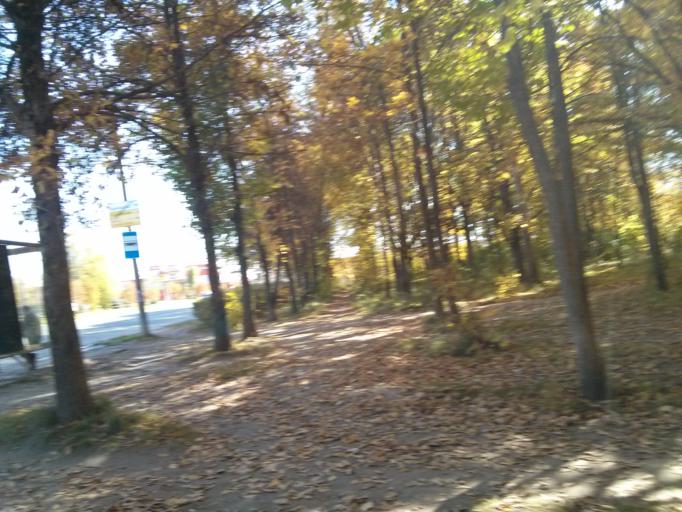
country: RU
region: Vladimir
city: Murom
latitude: 55.5489
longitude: 42.0634
